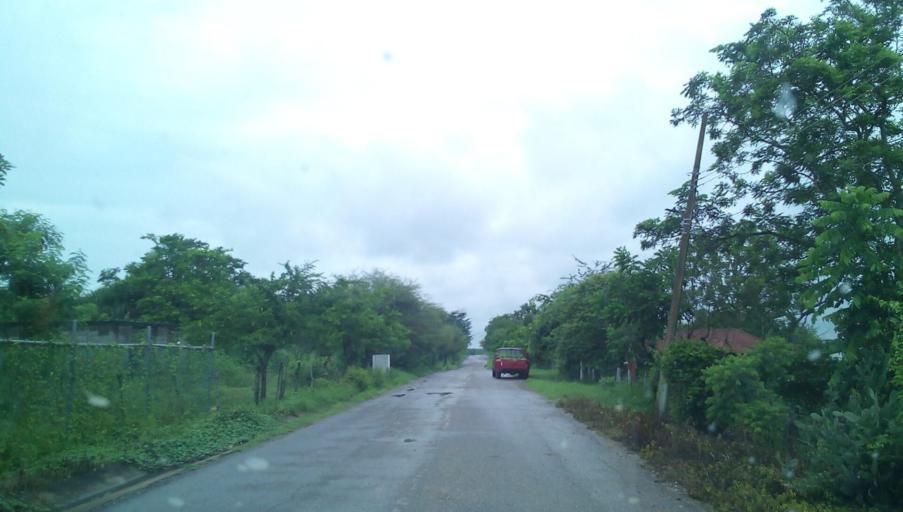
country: MX
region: Veracruz
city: Tempoal de Sanchez
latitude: 21.4649
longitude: -98.4214
